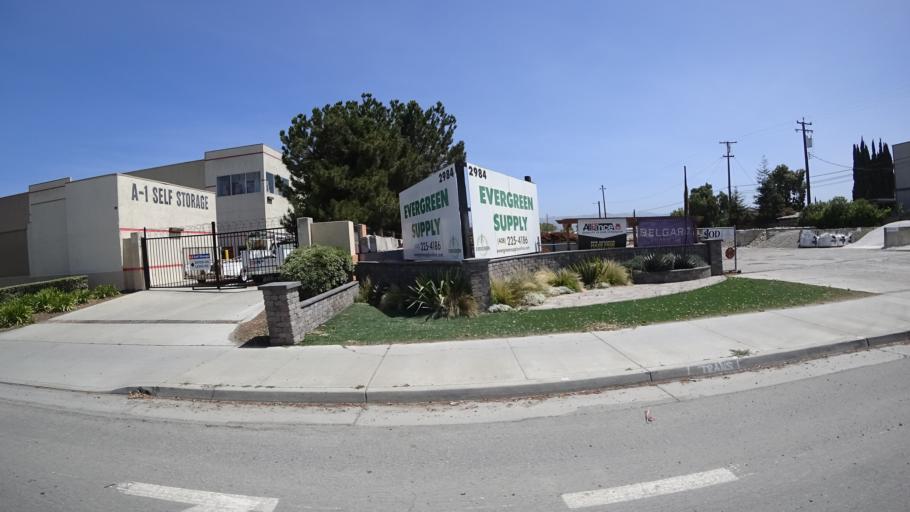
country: US
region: California
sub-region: Santa Clara County
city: Seven Trees
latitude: 37.2895
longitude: -121.8470
